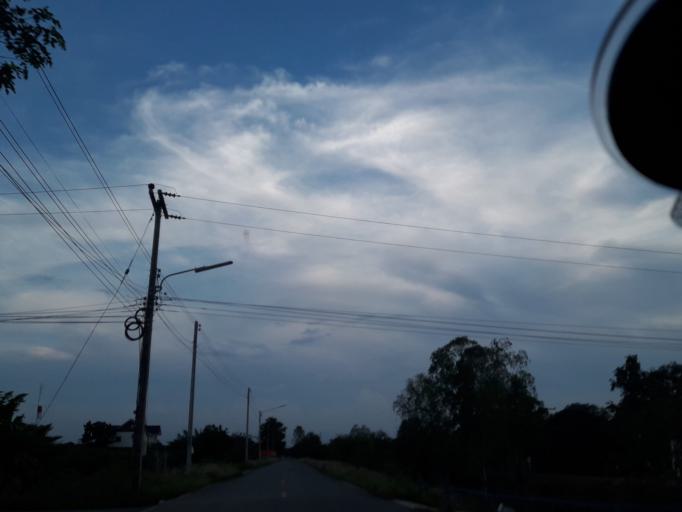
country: TH
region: Pathum Thani
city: Nong Suea
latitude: 14.2124
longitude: 100.8689
